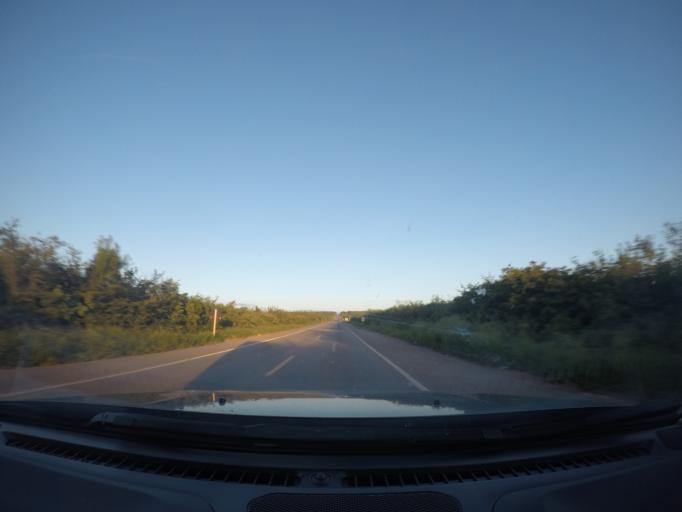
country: BR
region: Bahia
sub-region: Seabra
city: Seabra
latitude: -12.3928
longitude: -41.9205
